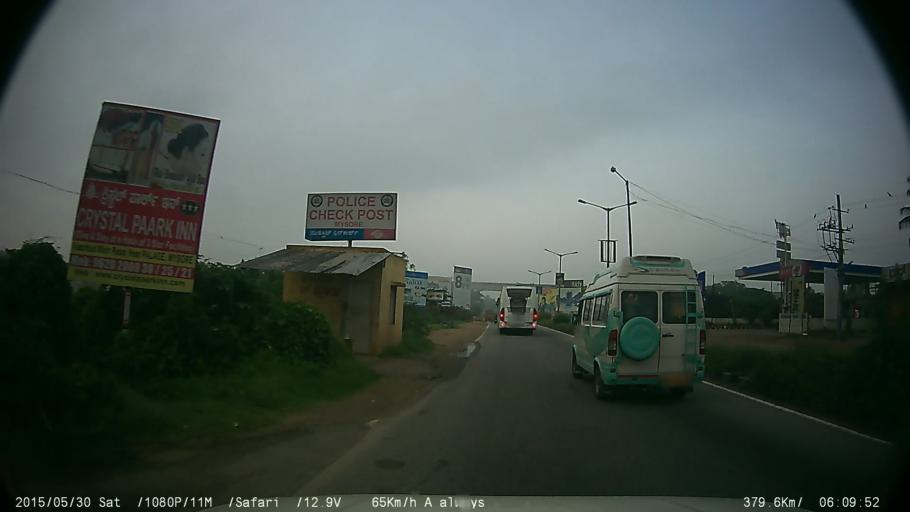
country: IN
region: Karnataka
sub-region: Mysore
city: Mysore
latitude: 12.3582
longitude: 76.6623
